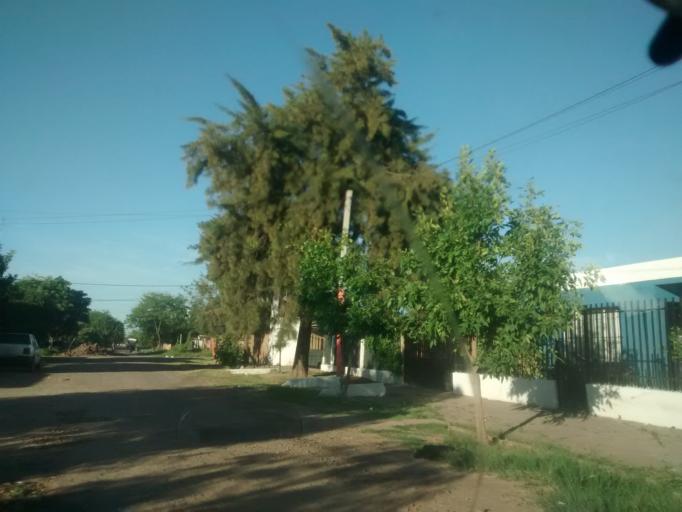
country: AR
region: Chaco
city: Resistencia
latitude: -27.4504
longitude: -59.0073
